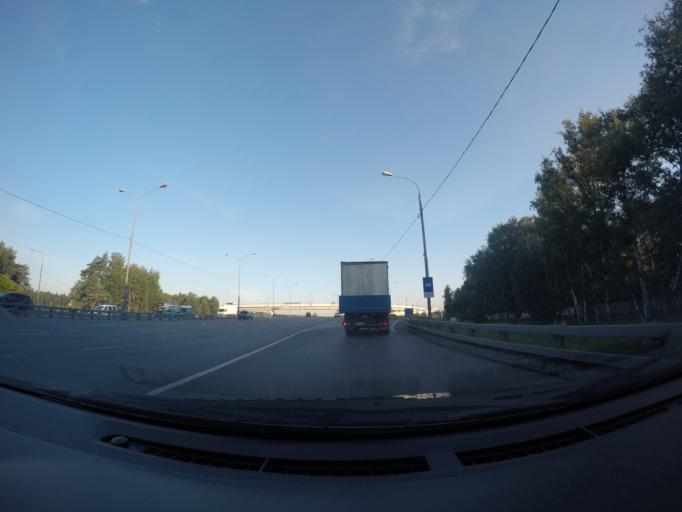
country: RU
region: Moscow
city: Zhulebino
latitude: 55.6850
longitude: 37.8363
